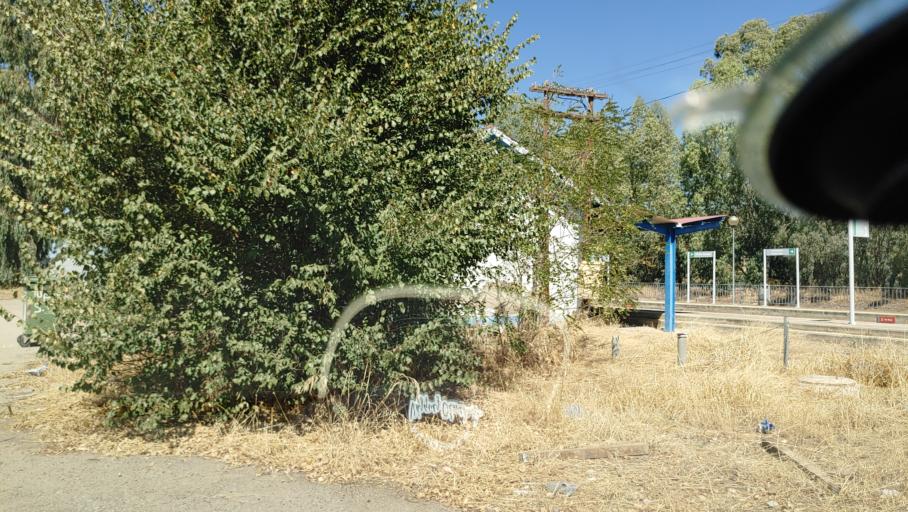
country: ES
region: Castille-La Mancha
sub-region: Provincia de Ciudad Real
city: Guadalmez
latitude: 38.6991
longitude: -4.9293
